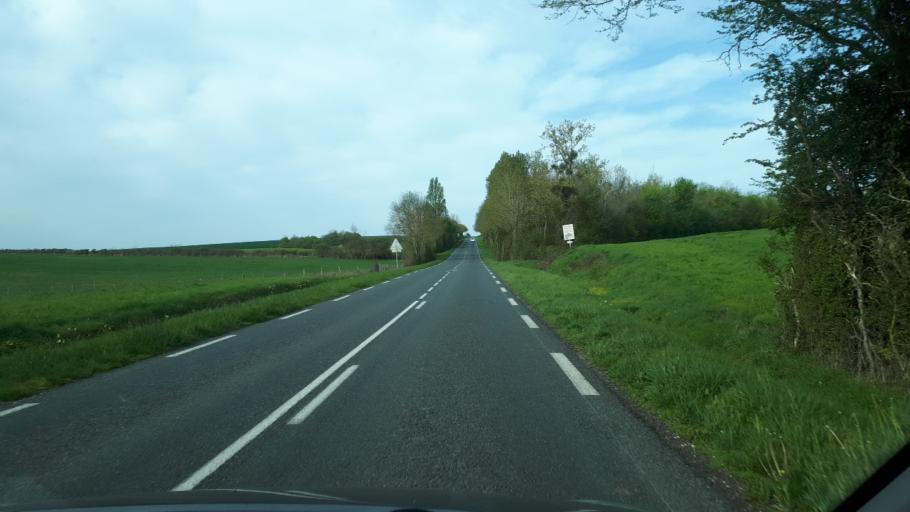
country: FR
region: Centre
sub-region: Departement du Cher
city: Sancerre
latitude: 47.2691
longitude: 2.7294
